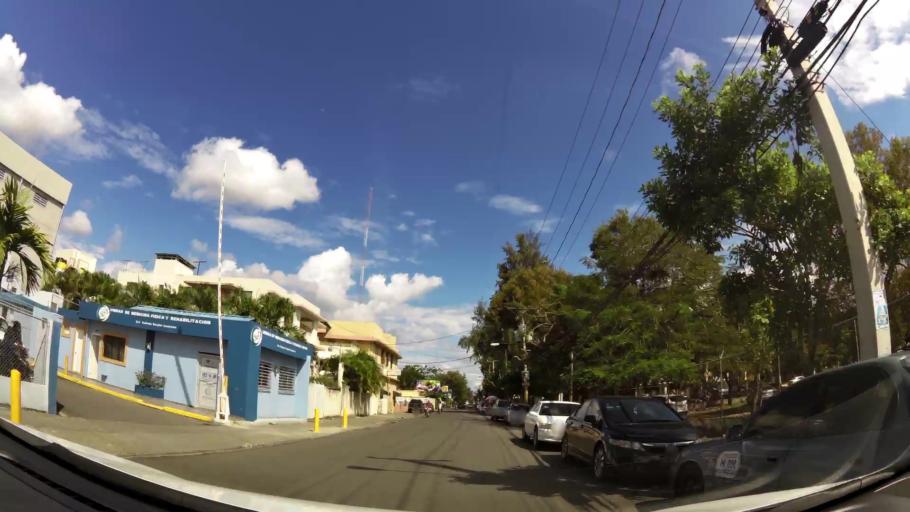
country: DO
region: La Vega
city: Concepcion de La Vega
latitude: 19.2220
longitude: -70.5287
